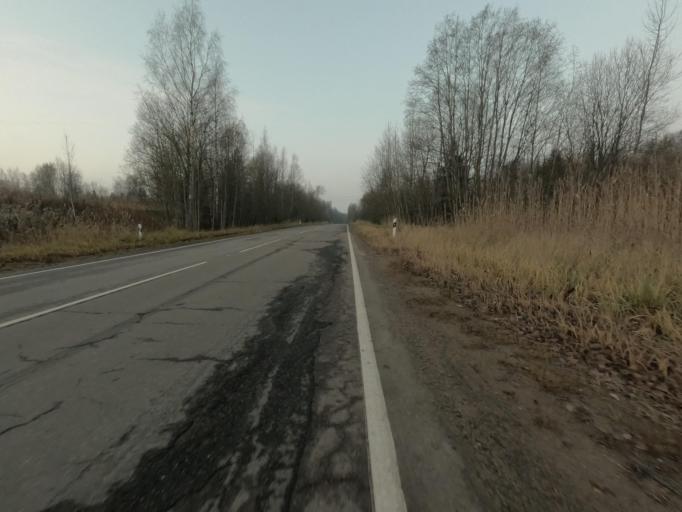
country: RU
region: Leningrad
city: Kirovsk
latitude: 59.8504
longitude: 30.9912
